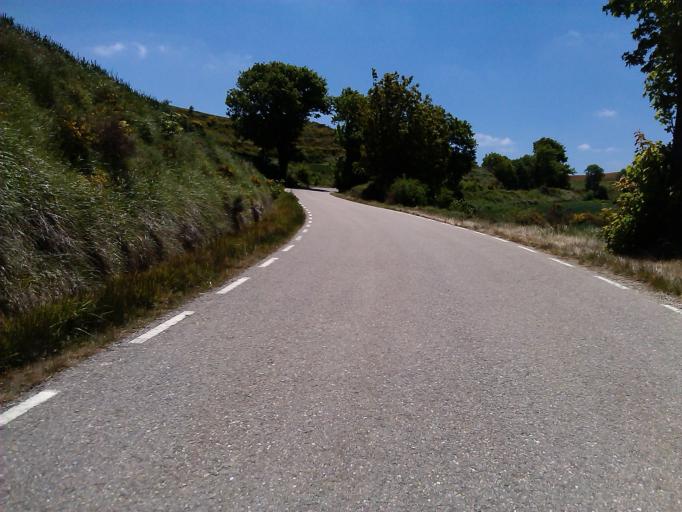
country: ES
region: Castille and Leon
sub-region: Provincia de Burgos
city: Cerraton de Juarros
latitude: 42.4269
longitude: -3.3631
